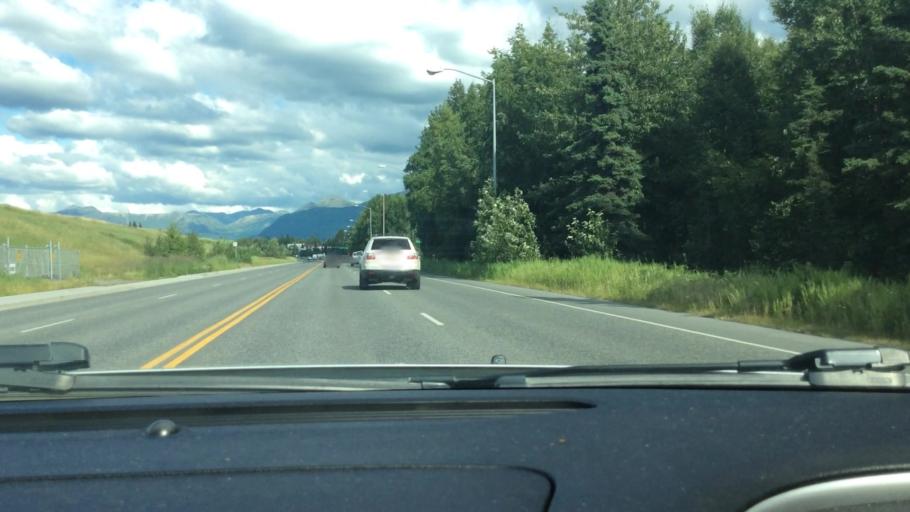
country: US
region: Alaska
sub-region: Anchorage Municipality
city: Anchorage
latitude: 61.2077
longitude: -149.8482
